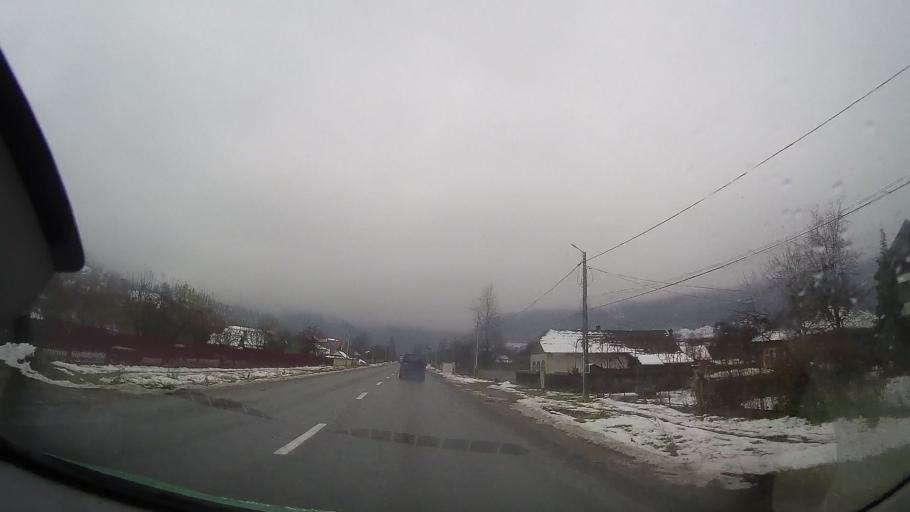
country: RO
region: Neamt
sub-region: Comuna Pangarati
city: Stejaru
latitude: 46.9063
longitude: 26.1765
